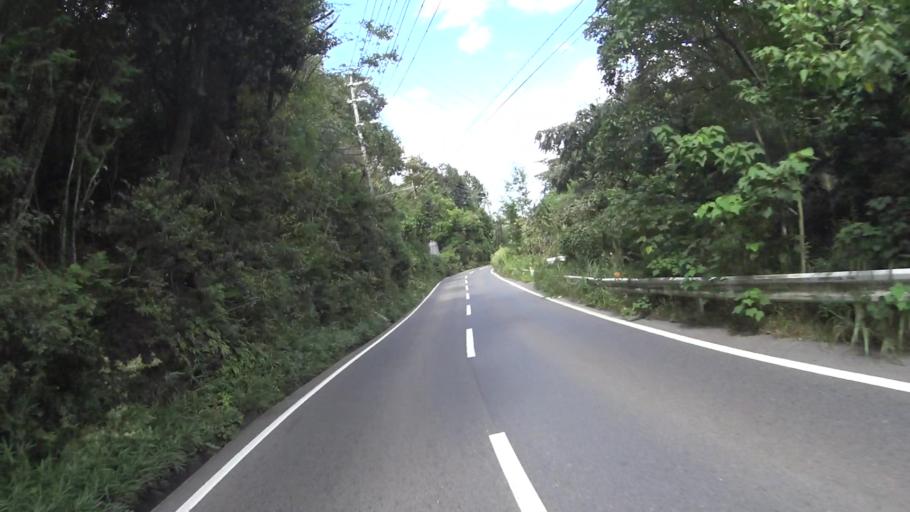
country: JP
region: Shiga Prefecture
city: Otsu-shi
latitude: 34.9363
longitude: 135.8902
